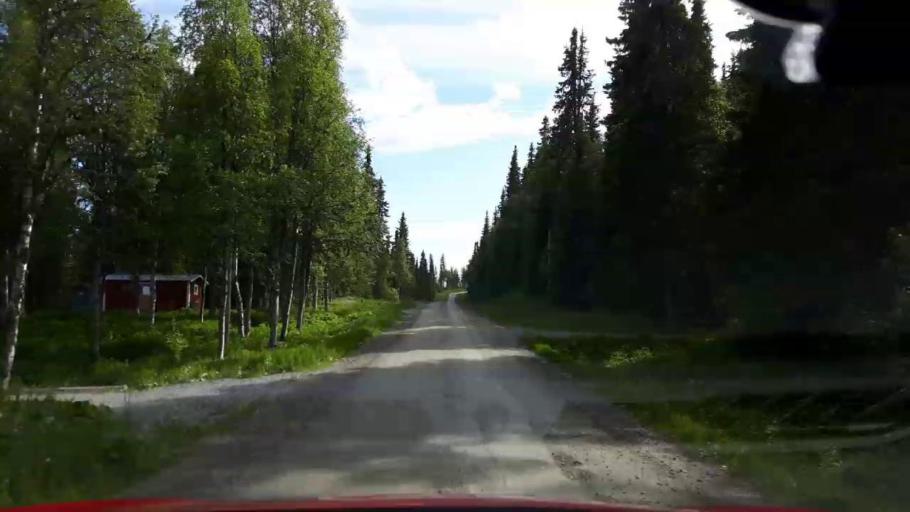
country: SE
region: Jaemtland
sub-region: Krokoms Kommun
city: Valla
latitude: 63.8469
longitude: 14.0785
